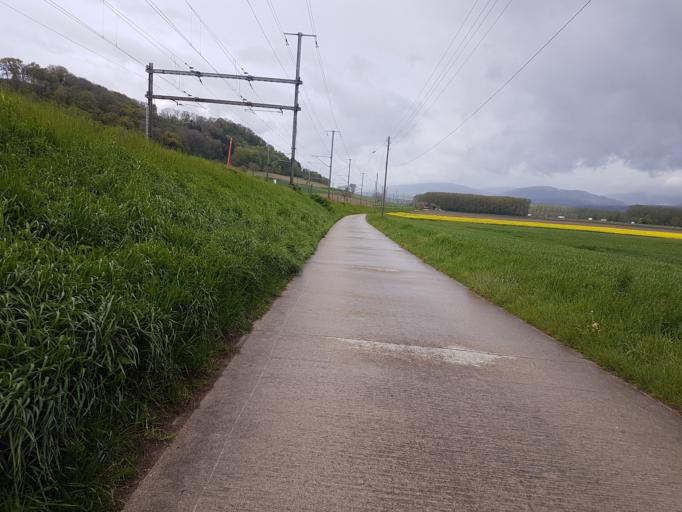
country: CH
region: Vaud
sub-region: Jura-Nord vaudois District
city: Montagny
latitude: 46.7453
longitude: 6.6050
